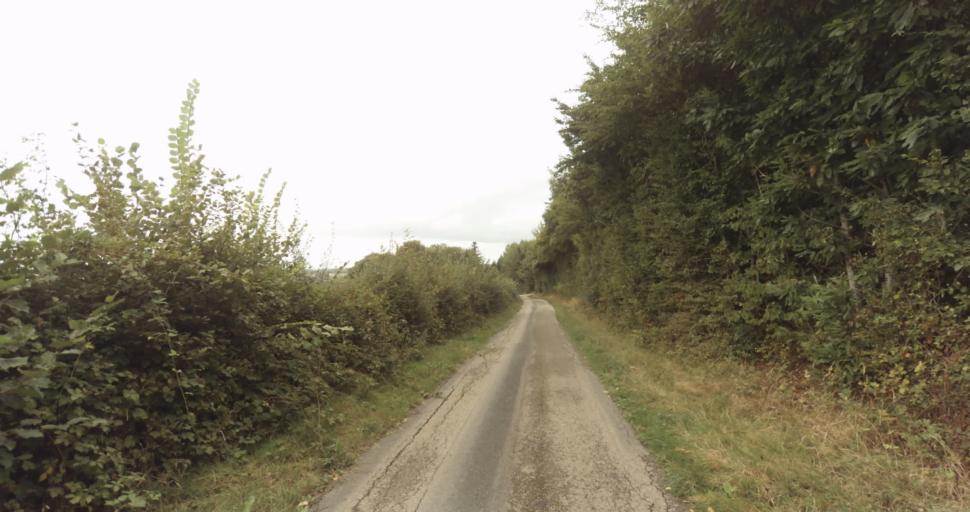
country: FR
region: Lower Normandy
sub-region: Departement de l'Orne
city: Gace
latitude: 48.7977
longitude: 0.3226
